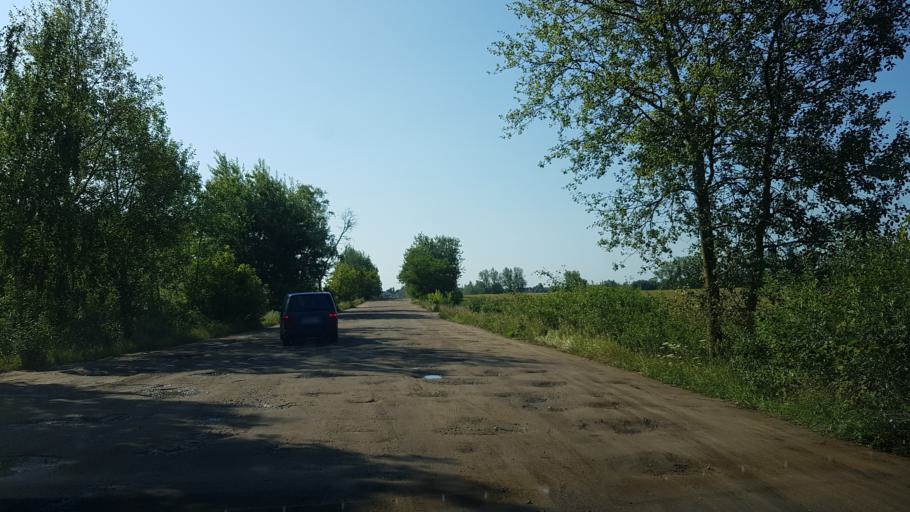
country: BY
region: Mogilev
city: Babruysk
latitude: 53.1188
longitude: 29.1877
